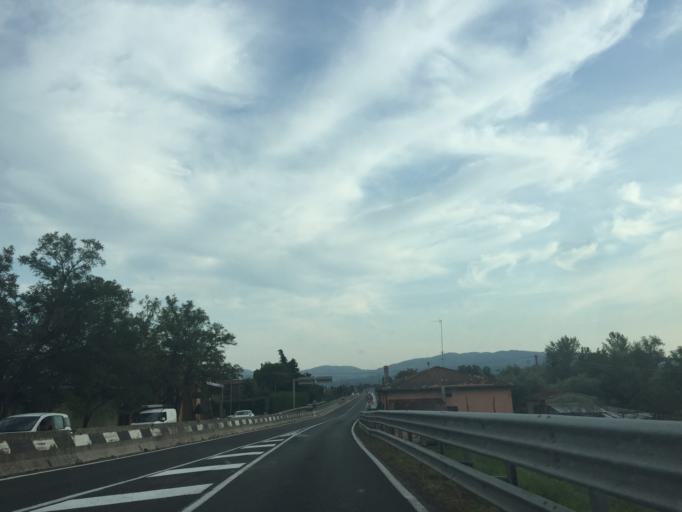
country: IT
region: Tuscany
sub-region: Provincia di Pistoia
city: Pistoia
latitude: 43.9556
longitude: 10.8982
